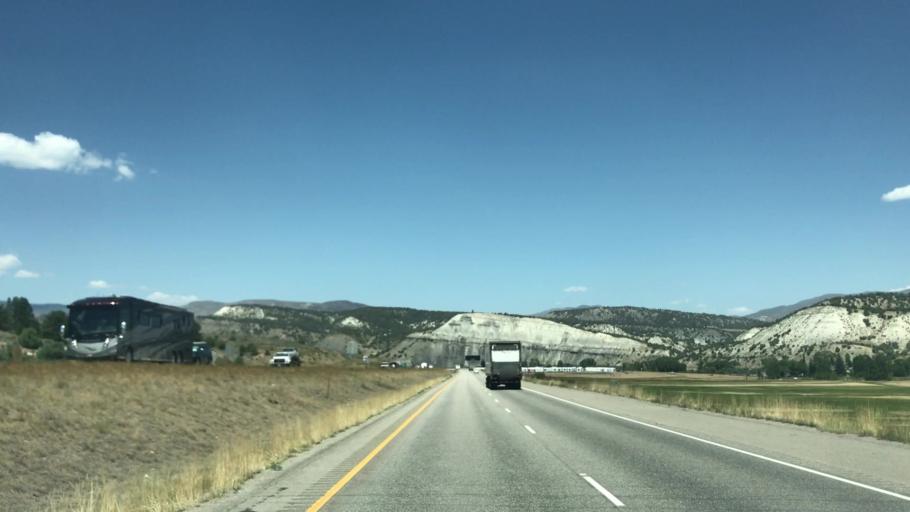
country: US
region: Colorado
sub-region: Eagle County
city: Edwards
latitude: 39.6883
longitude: -106.6623
